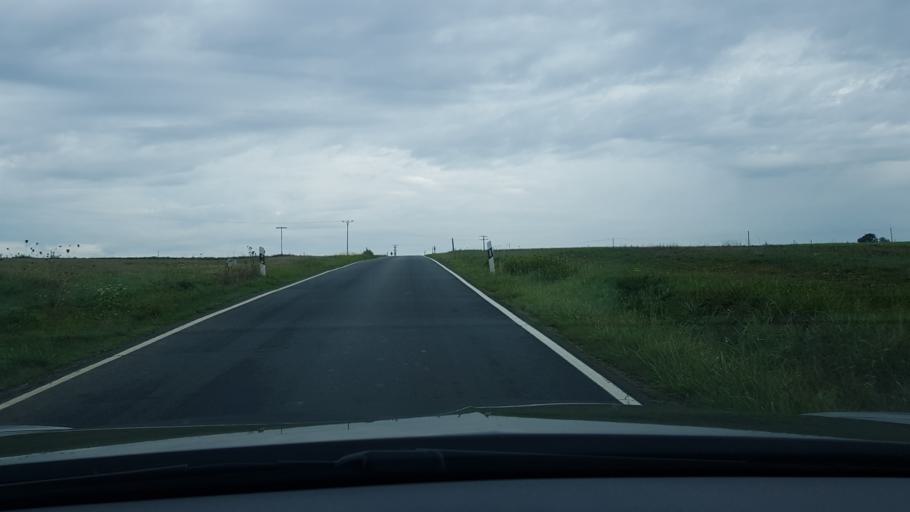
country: DE
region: Rheinland-Pfalz
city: Lof
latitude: 50.2339
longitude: 7.4270
